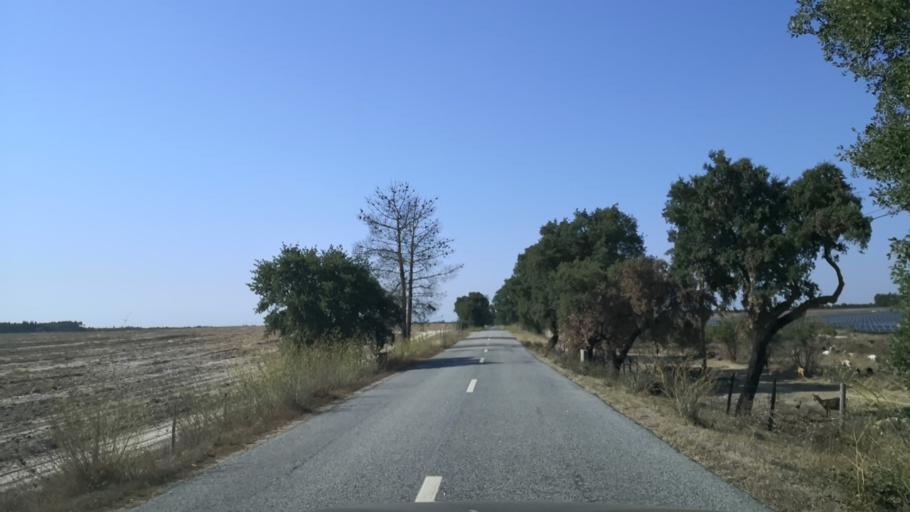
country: PT
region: Evora
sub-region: Vendas Novas
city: Vendas Novas
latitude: 38.7260
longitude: -8.6214
